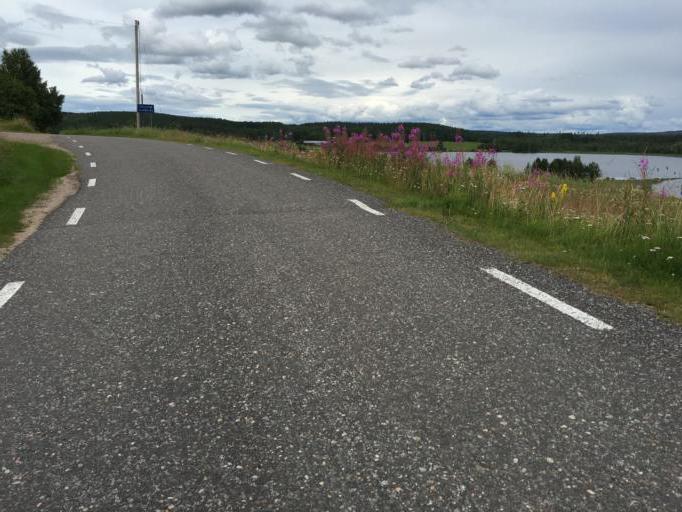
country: SE
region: Norrbotten
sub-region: Overkalix Kommun
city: OEverkalix
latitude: 66.1088
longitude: 22.7872
